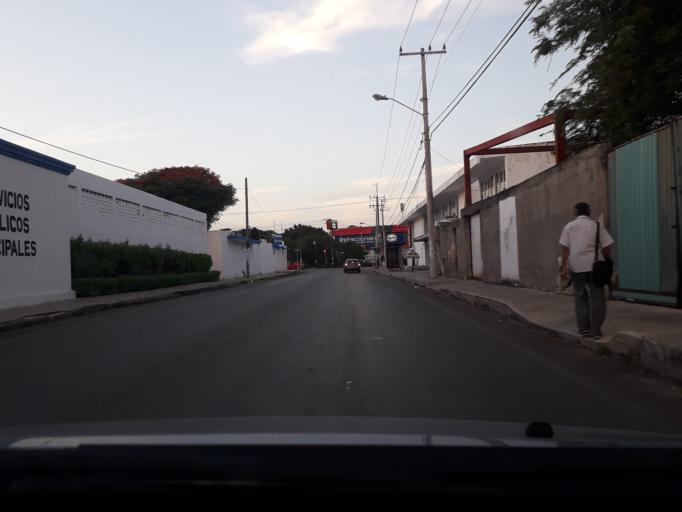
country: MX
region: Yucatan
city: Merida
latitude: 20.9831
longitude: -89.6548
